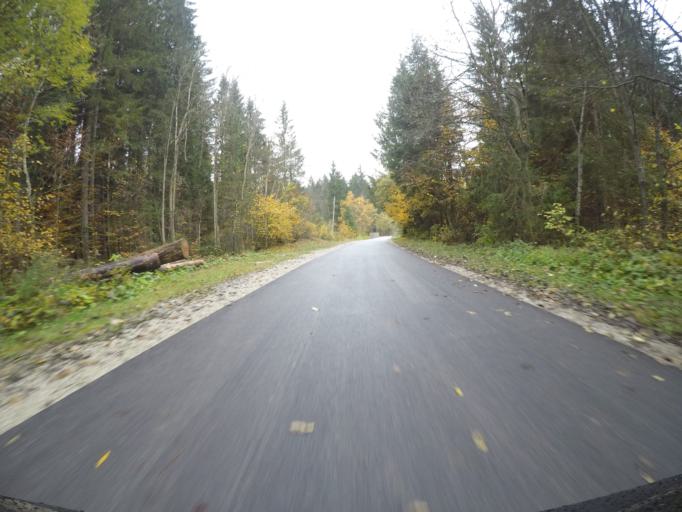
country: SI
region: Kranjska Gora
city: Kranjska Gora
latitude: 46.4901
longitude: 13.7345
